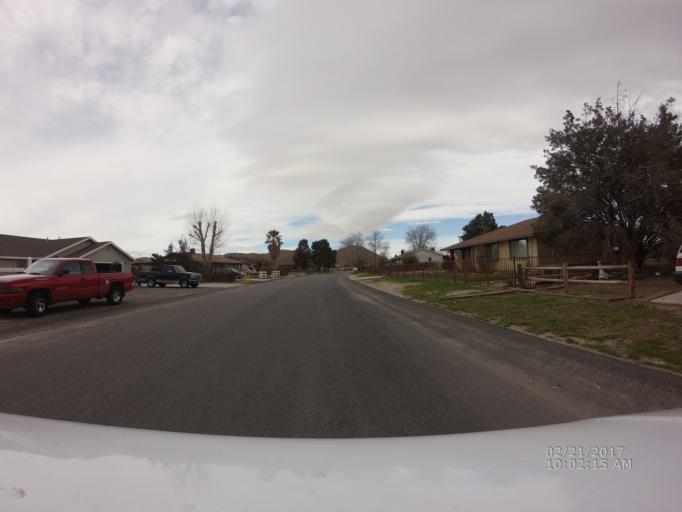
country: US
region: California
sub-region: Los Angeles County
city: Lake Los Angeles
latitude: 34.6006
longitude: -117.8224
